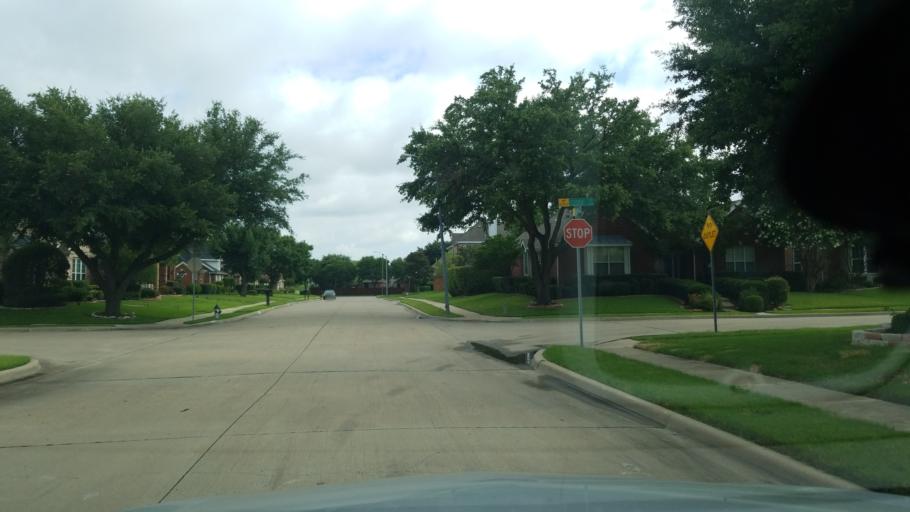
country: US
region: Texas
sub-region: Dallas County
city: Farmers Branch
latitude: 32.9448
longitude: -96.9486
